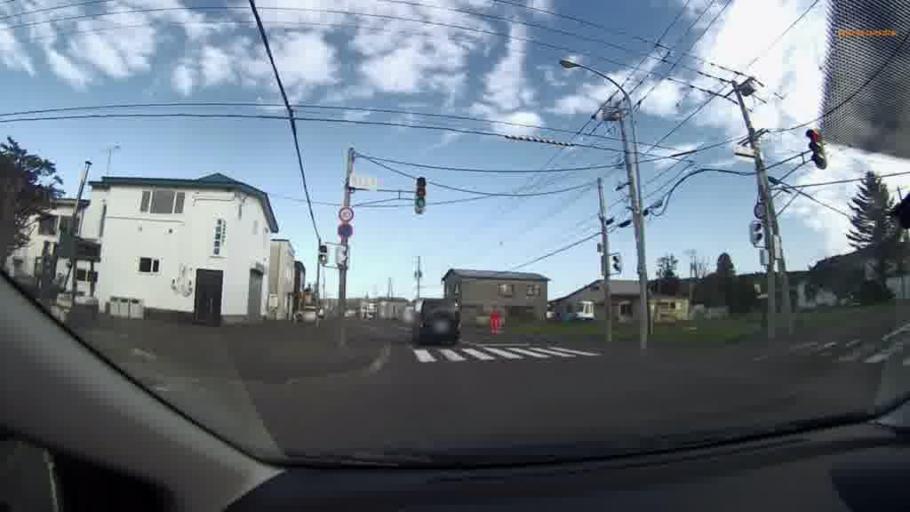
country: JP
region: Hokkaido
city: Kushiro
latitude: 42.9585
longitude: 144.0738
